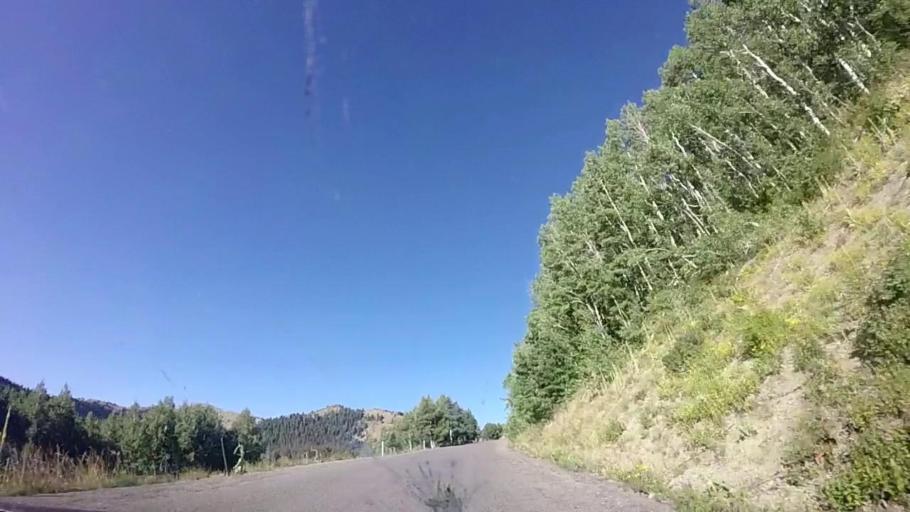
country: US
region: Utah
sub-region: Summit County
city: Park City
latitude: 40.6090
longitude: -111.5446
